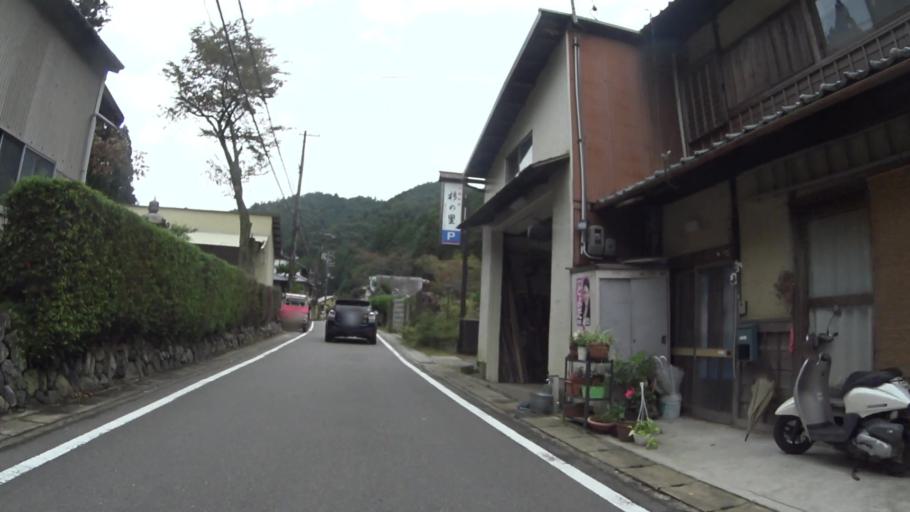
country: JP
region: Kyoto
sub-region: Kyoto-shi
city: Kamigyo-ku
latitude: 35.1117
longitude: 135.7711
